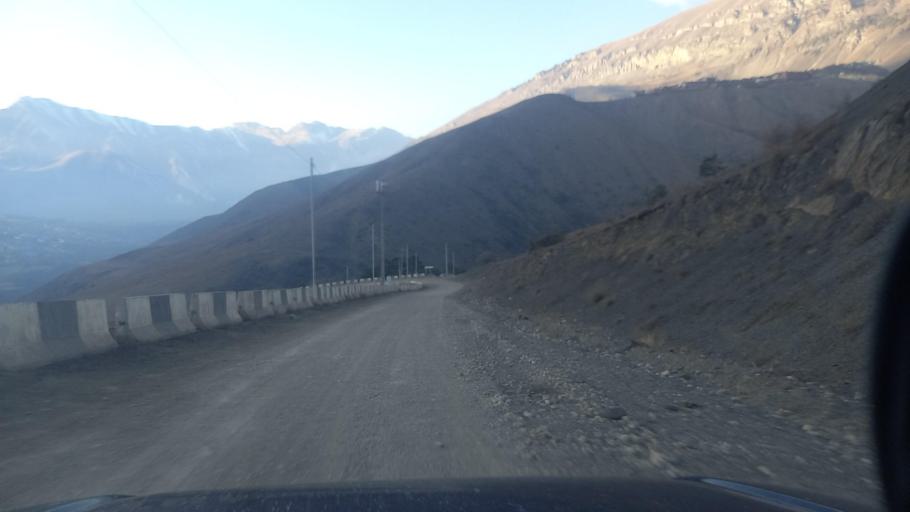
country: RU
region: Ingushetiya
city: Dzhayrakh
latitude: 42.8193
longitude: 44.7041
